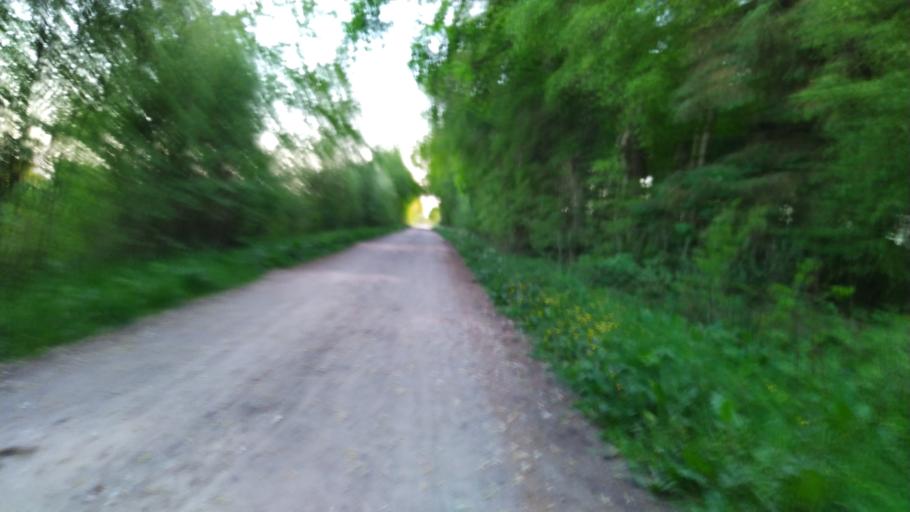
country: DE
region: Lower Saxony
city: Bargstedt
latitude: 53.4871
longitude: 9.4545
